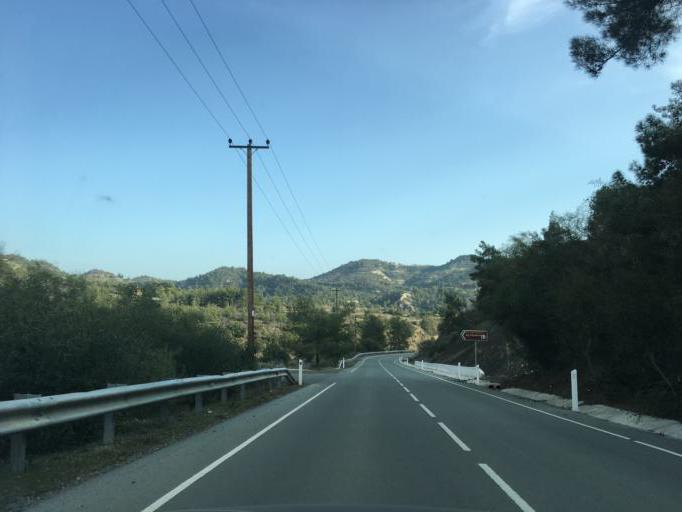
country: CY
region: Limassol
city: Pelendri
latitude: 34.8282
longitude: 32.9636
